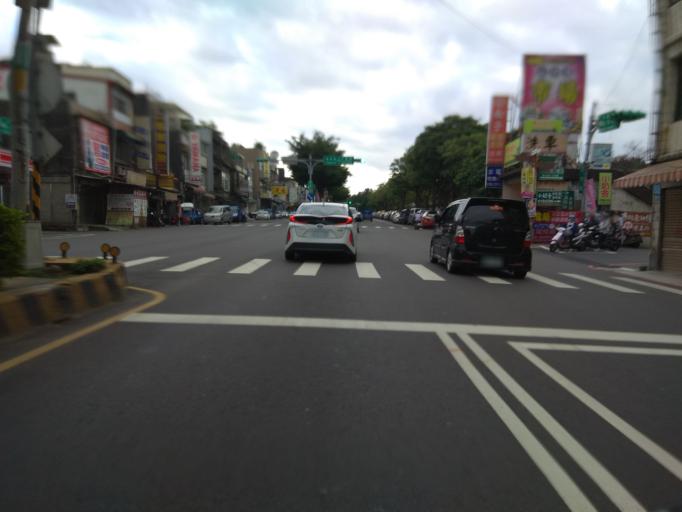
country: TW
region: Taiwan
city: Daxi
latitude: 24.8964
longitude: 121.2111
